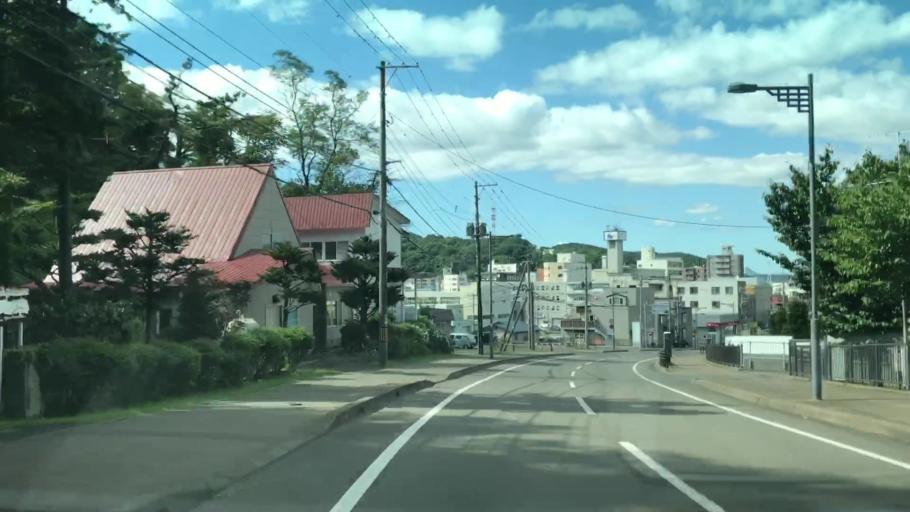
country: JP
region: Hokkaido
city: Muroran
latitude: 42.3127
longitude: 140.9760
